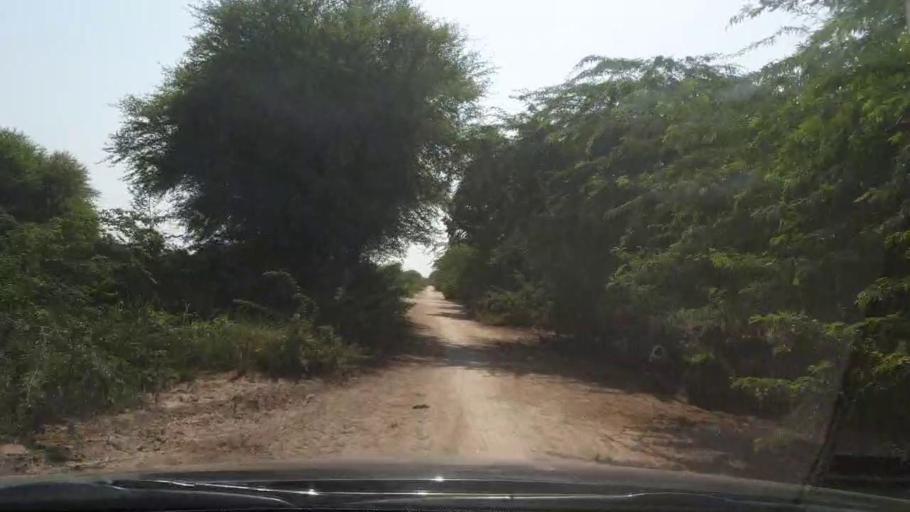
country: PK
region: Sindh
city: Naukot
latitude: 24.8050
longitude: 69.2565
